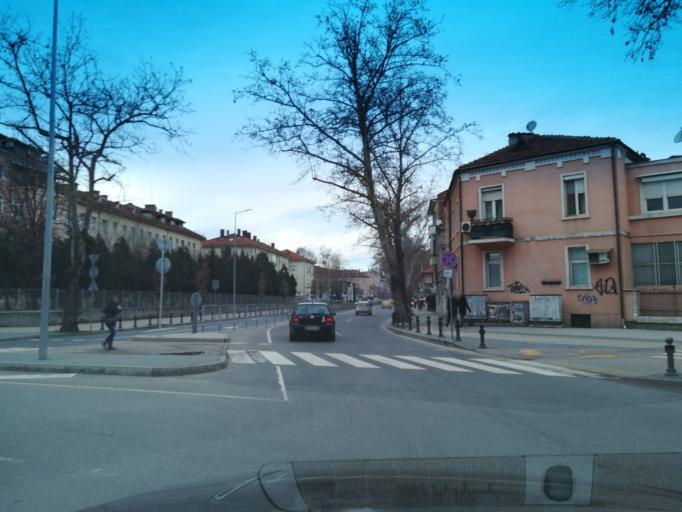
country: BG
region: Plovdiv
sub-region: Obshtina Plovdiv
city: Plovdiv
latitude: 42.1389
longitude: 24.7386
